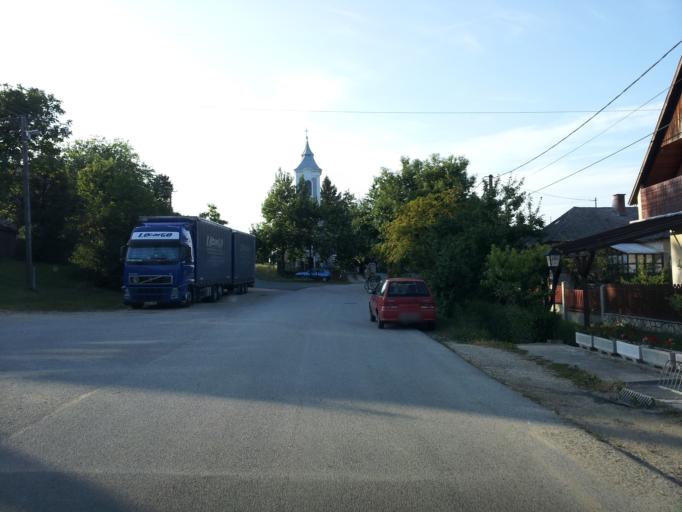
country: HU
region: Veszprem
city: Ajka
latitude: 46.9810
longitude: 17.5681
